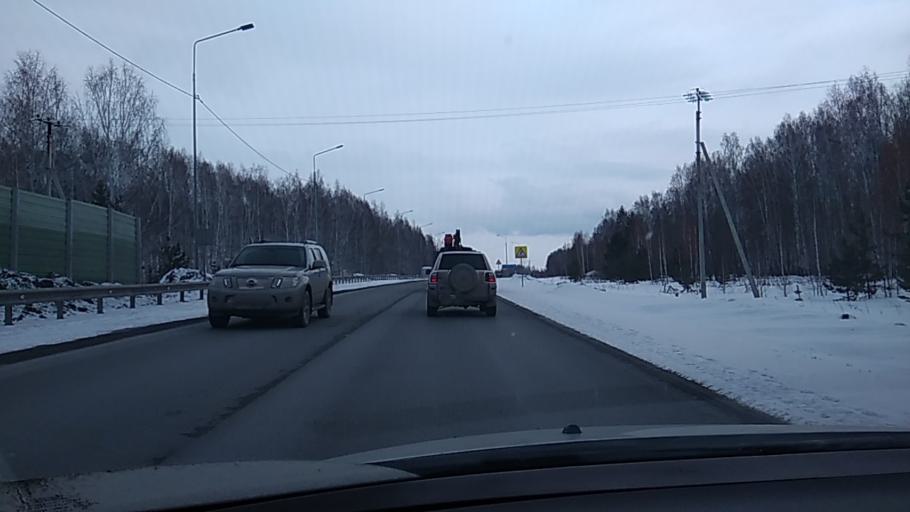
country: RU
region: Sverdlovsk
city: Sovkhoznyy
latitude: 56.5226
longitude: 61.4346
